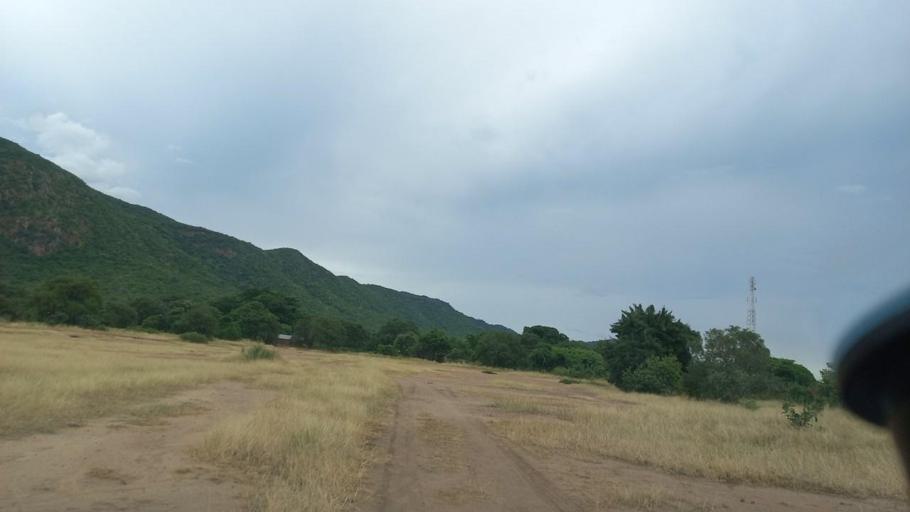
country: ZM
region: Lusaka
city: Luangwa
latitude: -15.6179
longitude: 30.2656
